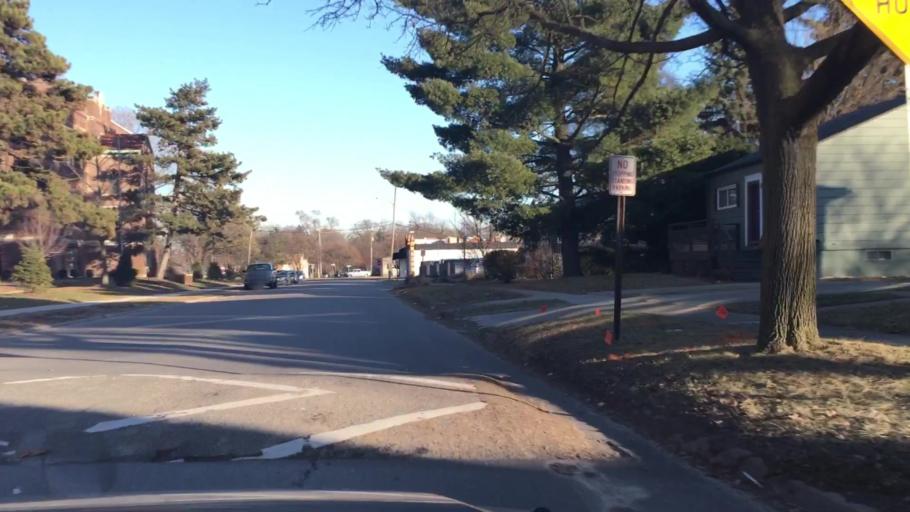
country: US
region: Michigan
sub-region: Oakland County
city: Ferndale
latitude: 42.4555
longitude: -83.1331
